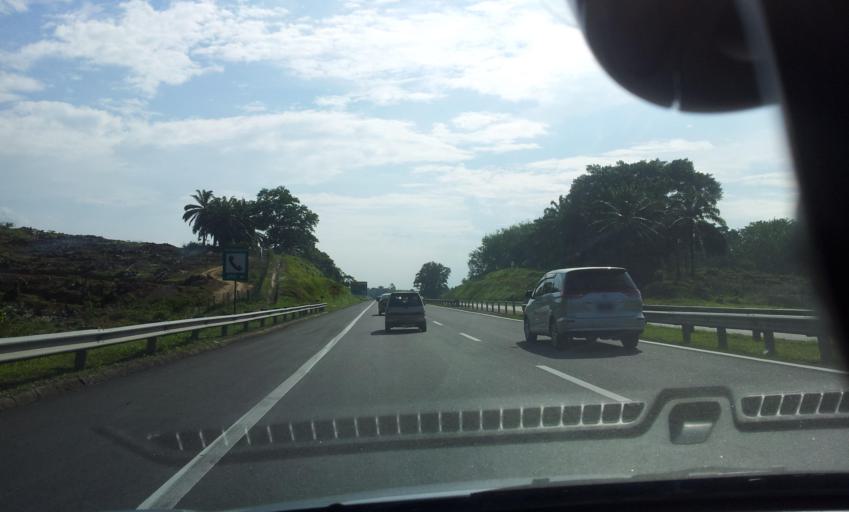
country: MY
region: Pahang
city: Mentekab
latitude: 3.5314
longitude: 102.2011
